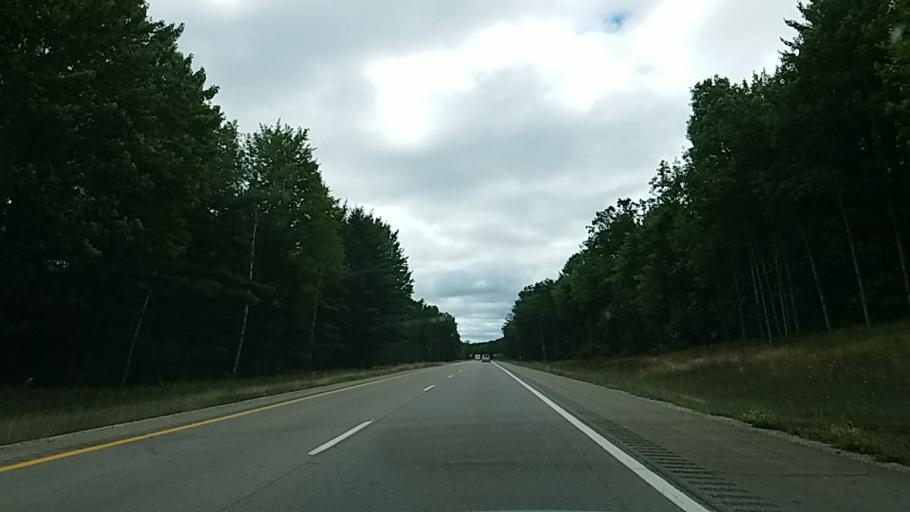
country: US
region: Michigan
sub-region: Crawford County
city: Grayling
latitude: 44.7399
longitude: -84.7095
